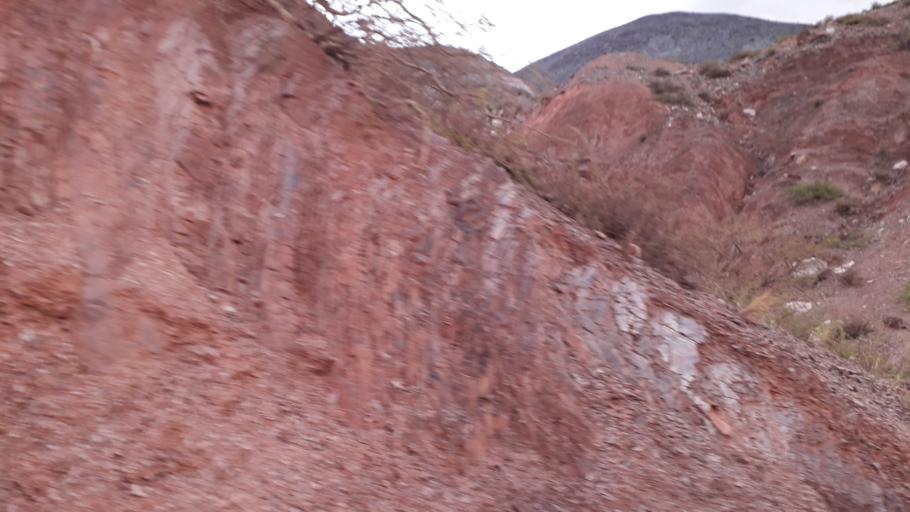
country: AR
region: Jujuy
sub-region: Departamento de Tumbaya
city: Tumbaya
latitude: -23.7472
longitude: -65.5076
